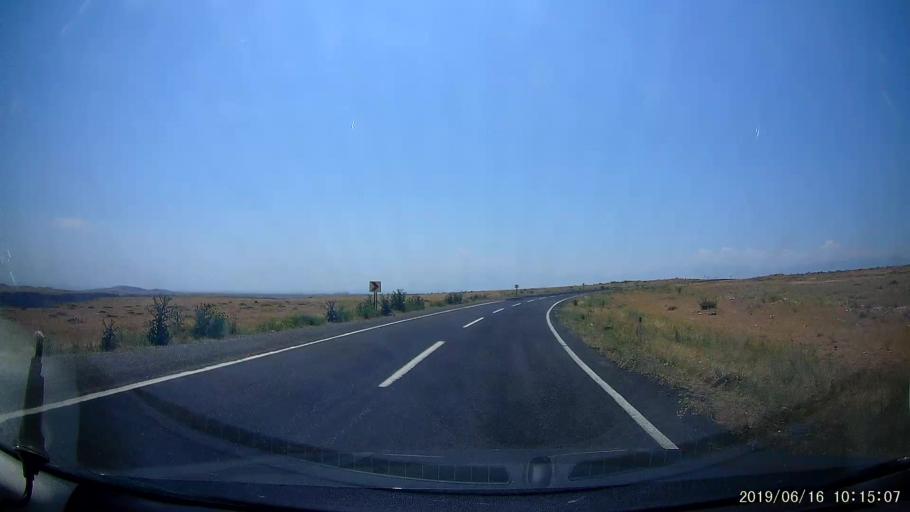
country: TR
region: Igdir
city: Tuzluca
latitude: 40.1789
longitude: 43.6763
